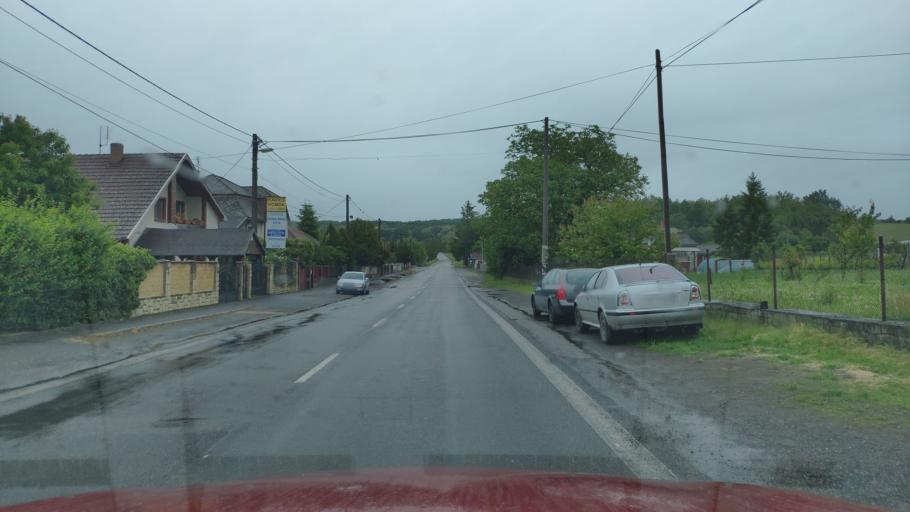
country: HU
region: Borsod-Abauj-Zemplen
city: Ricse
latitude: 48.4354
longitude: 21.9253
